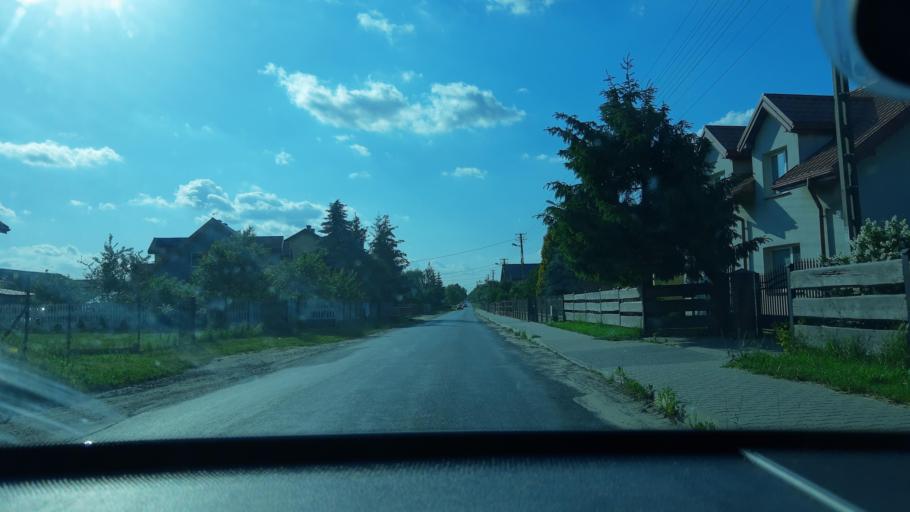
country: PL
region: Lodz Voivodeship
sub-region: Powiat sieradzki
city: Sieradz
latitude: 51.5476
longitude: 18.7778
